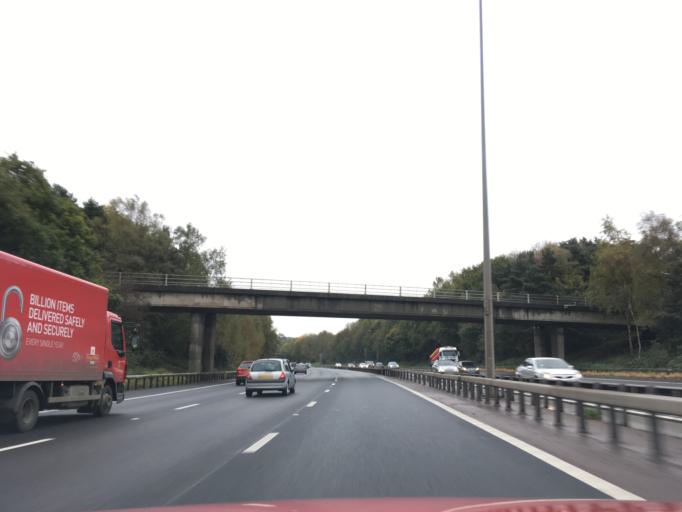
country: GB
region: England
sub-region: Hampshire
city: Bursledon
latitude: 50.8931
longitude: -1.3083
